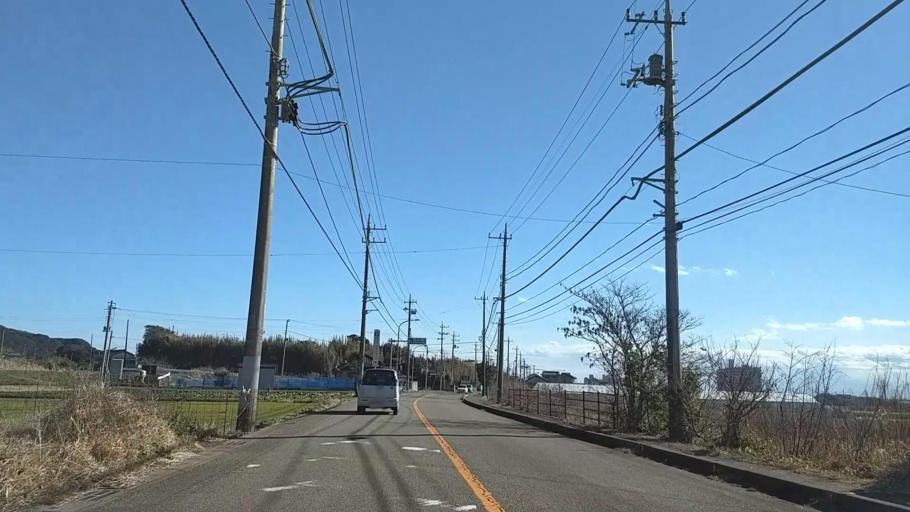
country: JP
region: Chiba
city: Tateyama
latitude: 34.9091
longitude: 139.8756
